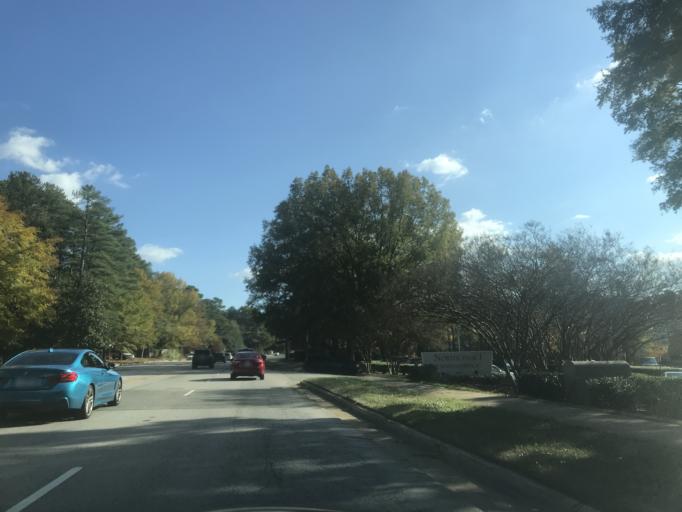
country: US
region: North Carolina
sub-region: Wake County
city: West Raleigh
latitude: 35.8694
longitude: -78.6399
